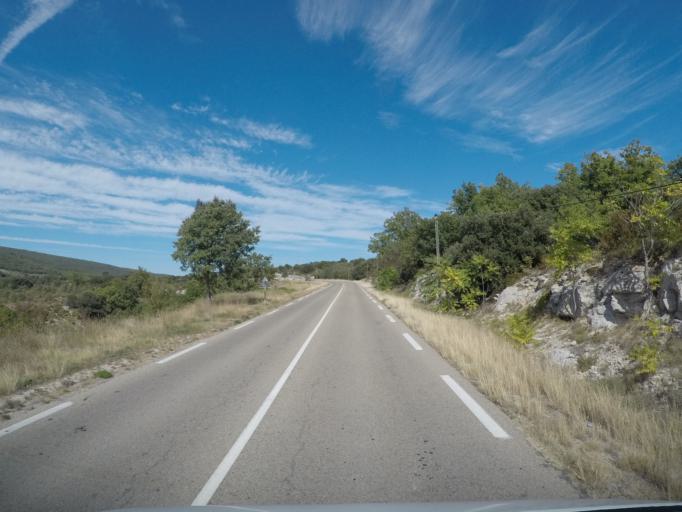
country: FR
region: Languedoc-Roussillon
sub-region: Departement de l'Herault
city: Saint-Martin-de-Londres
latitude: 43.8167
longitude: 3.7439
